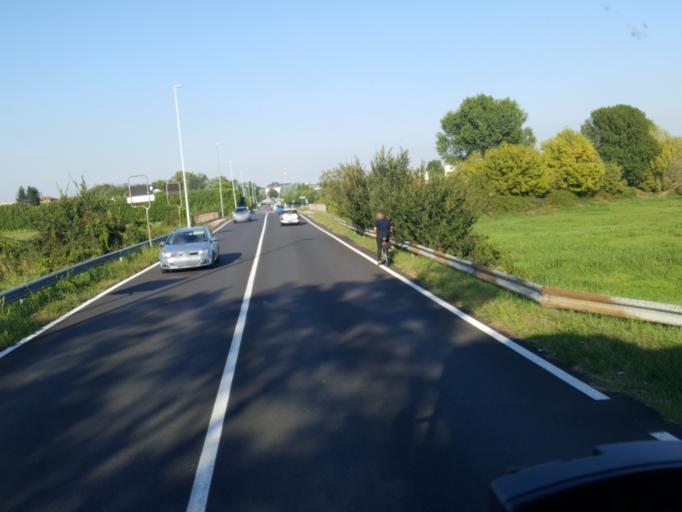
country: IT
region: Lombardy
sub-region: Citta metropolitana di Milano
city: Parabiago
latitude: 45.5689
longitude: 8.9525
